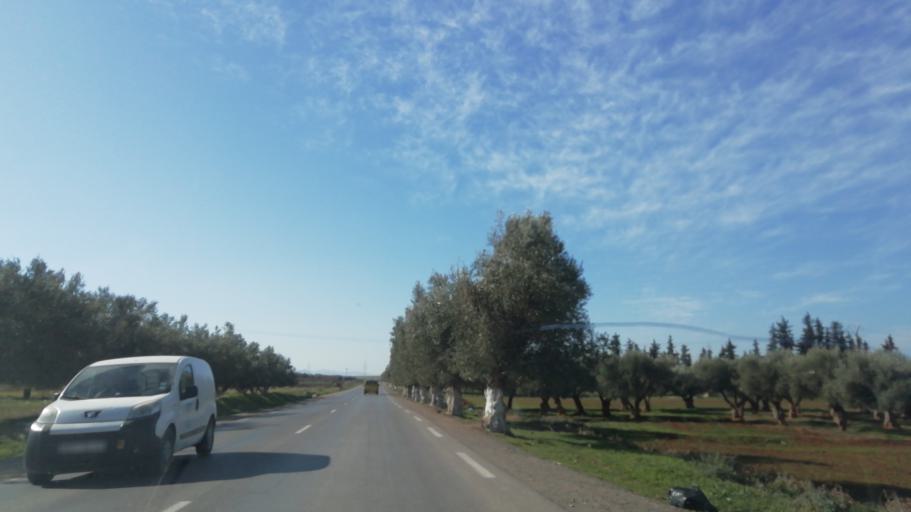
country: DZ
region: Tlemcen
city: Ouled Mimoun
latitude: 35.0230
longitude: -0.8975
